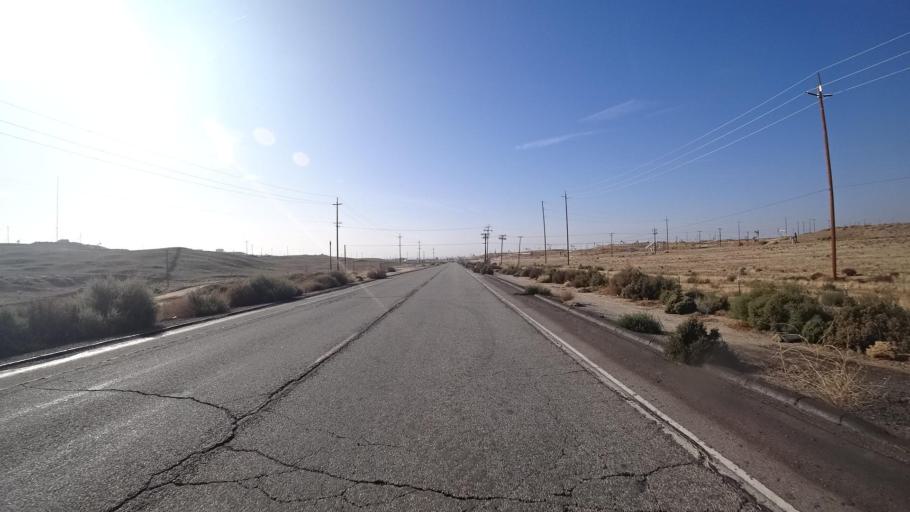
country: US
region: California
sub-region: Kern County
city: Oildale
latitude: 35.4711
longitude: -119.0229
